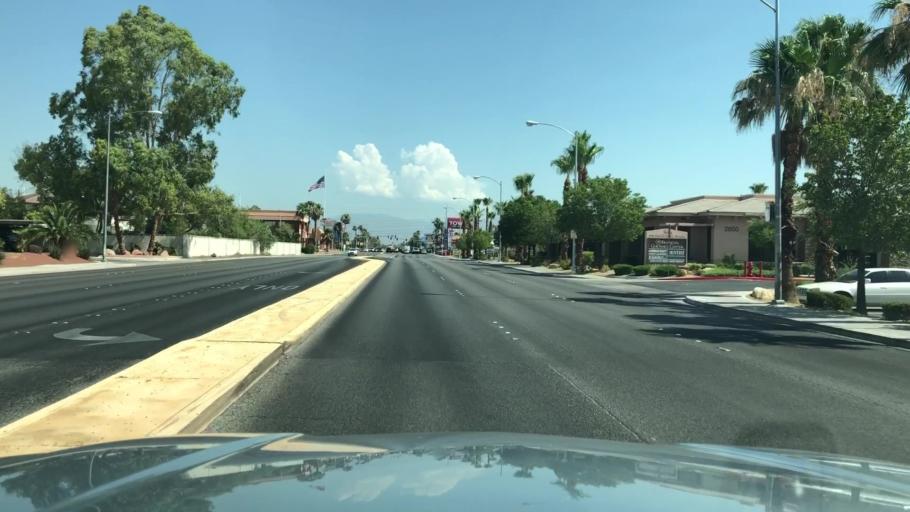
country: US
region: Nevada
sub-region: Clark County
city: Spring Valley
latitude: 36.1407
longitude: -115.2252
